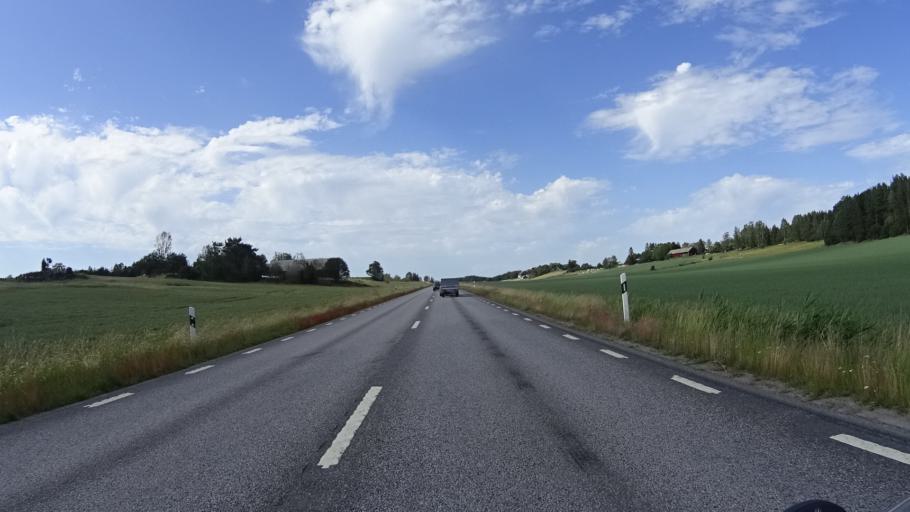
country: SE
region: OEstergoetland
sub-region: Linkopings Kommun
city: Sturefors
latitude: 58.3378
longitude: 15.8482
